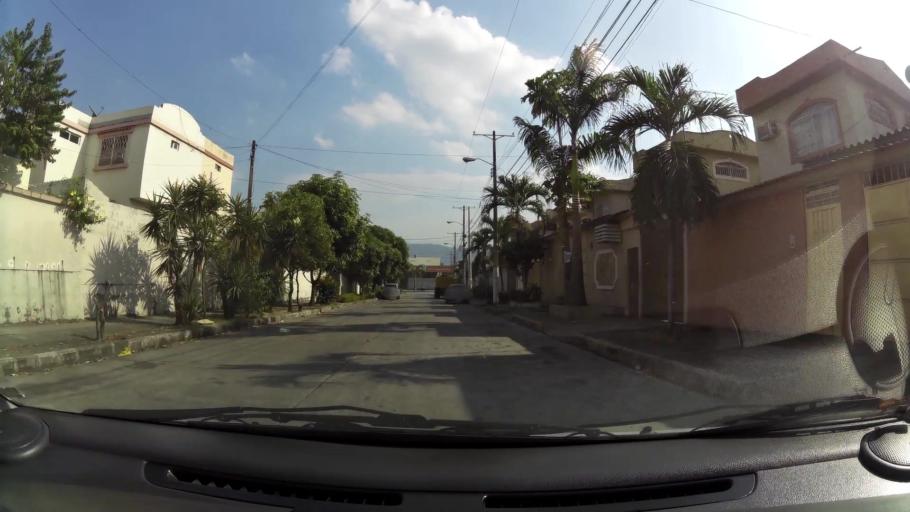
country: EC
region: Guayas
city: Guayaquil
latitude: -2.1330
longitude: -79.9285
